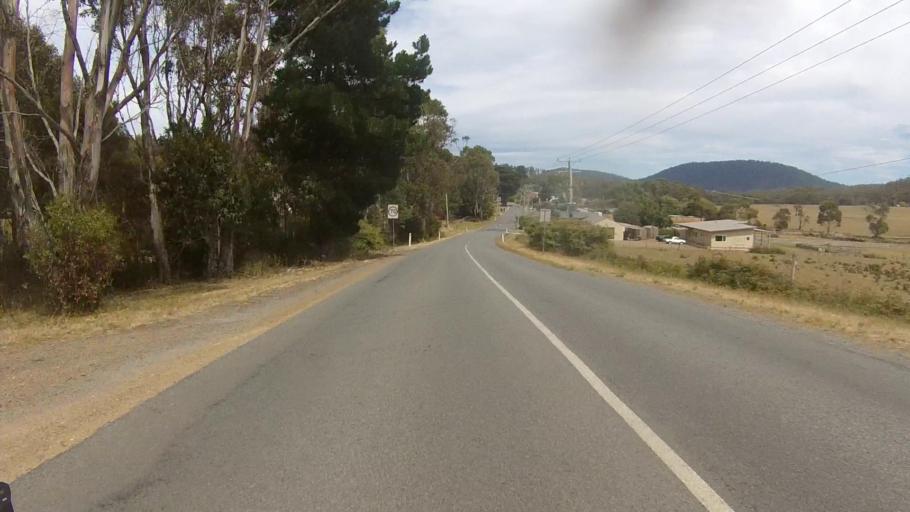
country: AU
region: Tasmania
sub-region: Sorell
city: Sorell
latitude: -42.8192
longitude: 147.8070
